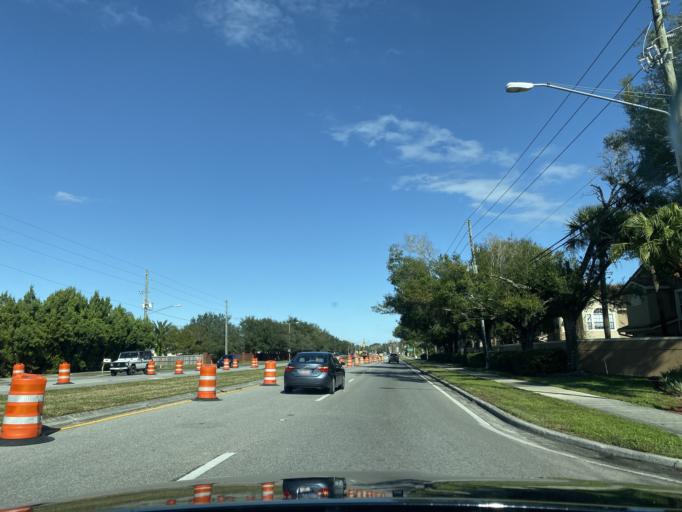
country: US
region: Florida
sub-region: Orange County
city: Alafaya
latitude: 28.5929
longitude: -81.2448
